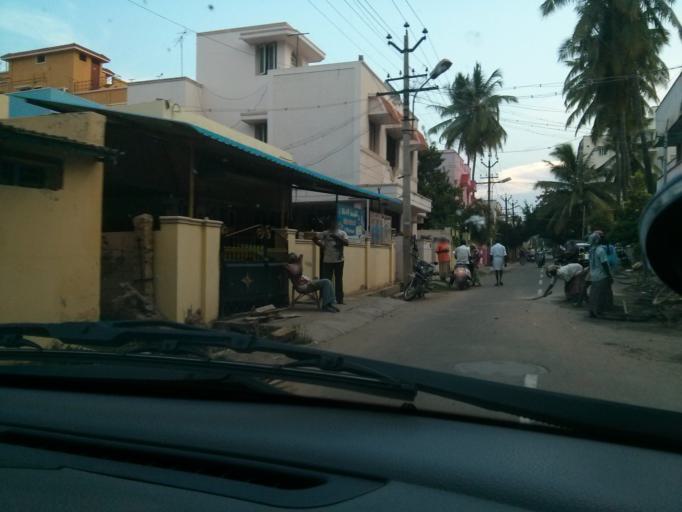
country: IN
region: Tamil Nadu
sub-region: Coimbatore
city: Coimbatore
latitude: 11.0323
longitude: 76.9438
